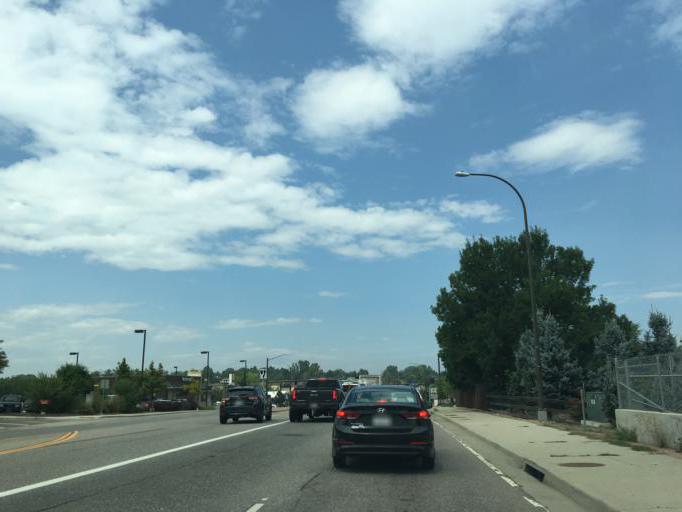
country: US
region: Colorado
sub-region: Jefferson County
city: Wheat Ridge
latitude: 39.7387
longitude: -105.1095
